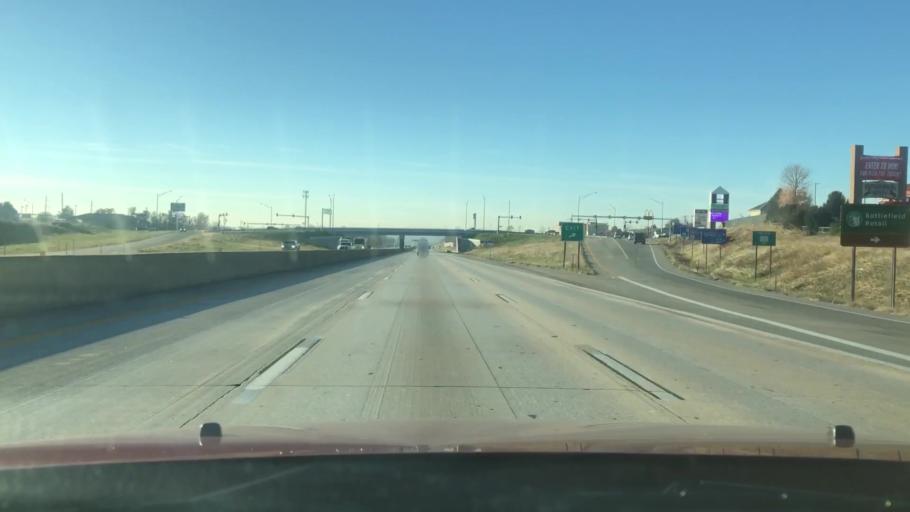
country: US
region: Missouri
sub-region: Greene County
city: Springfield
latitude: 37.1609
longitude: -93.2247
